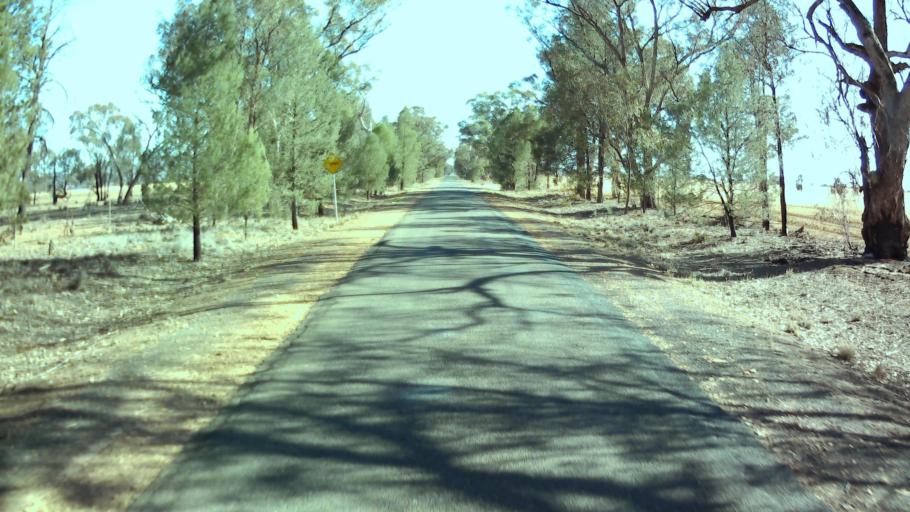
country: AU
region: New South Wales
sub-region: Weddin
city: Grenfell
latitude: -33.8082
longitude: 147.9545
